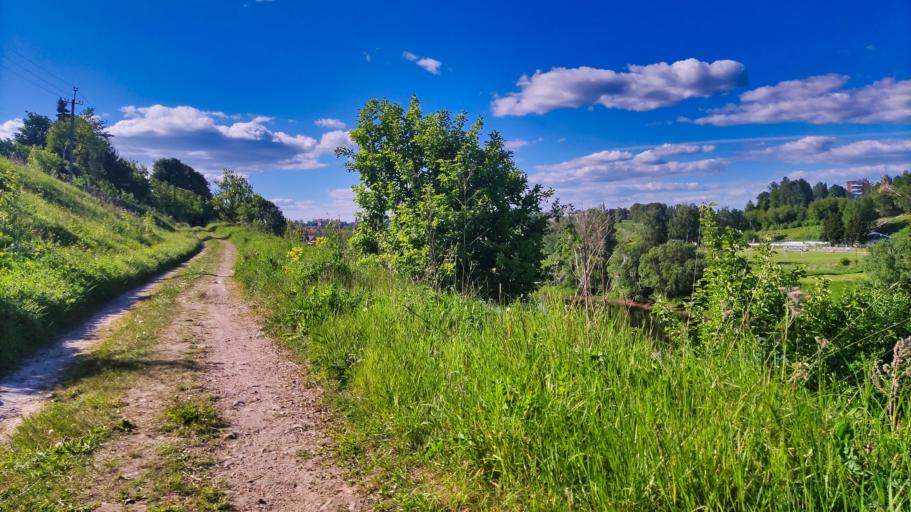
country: RU
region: Tverskaya
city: Rzhev
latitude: 56.2523
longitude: 34.3431
